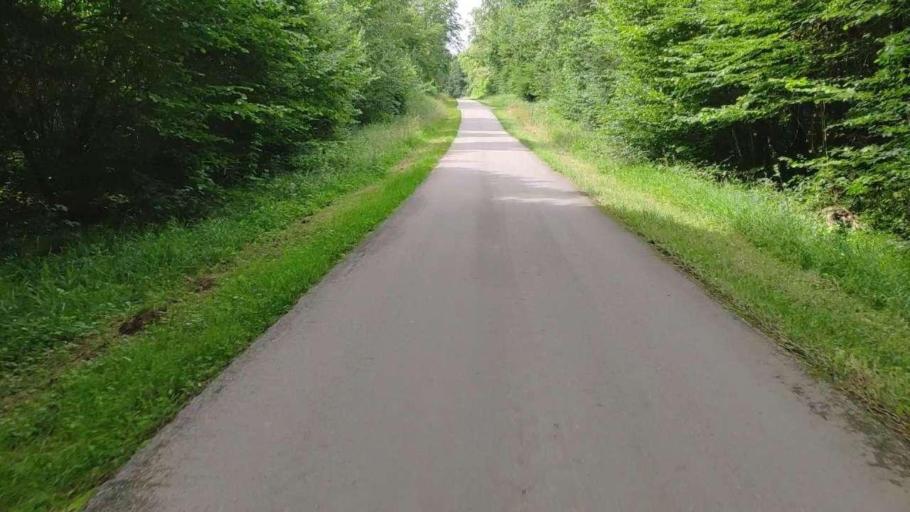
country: FR
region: Franche-Comte
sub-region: Departement du Jura
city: Bletterans
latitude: 46.8091
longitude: 5.4405
